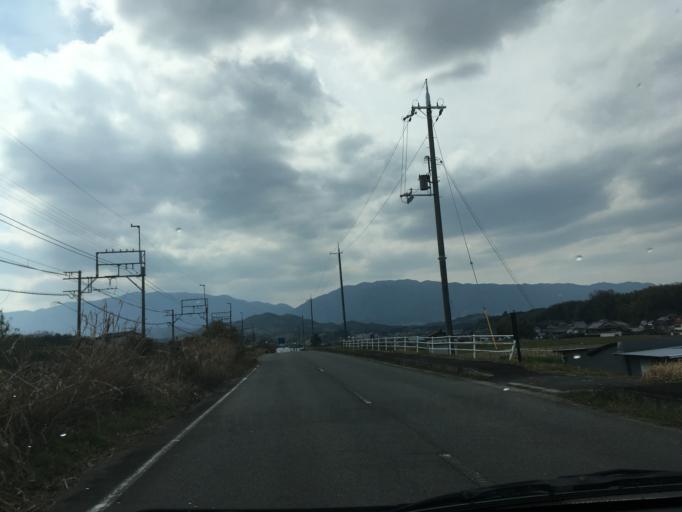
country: JP
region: Nara
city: Gose
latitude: 34.4469
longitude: 135.7882
